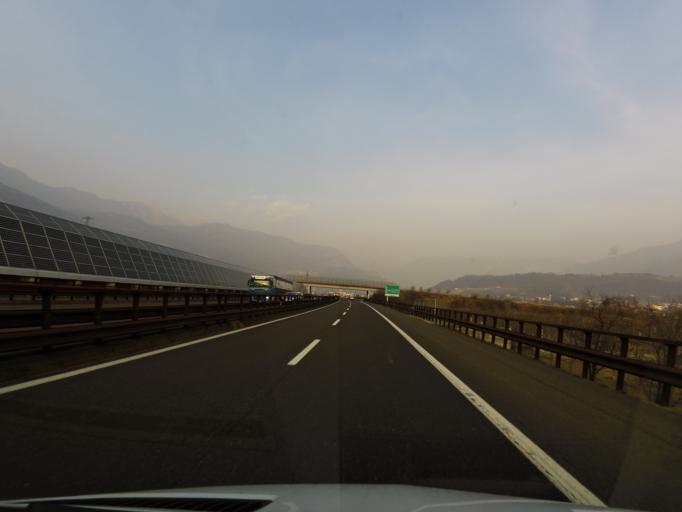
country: IT
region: Trentino-Alto Adige
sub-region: Provincia di Trento
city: Nogaredo
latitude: 45.8986
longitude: 11.0234
